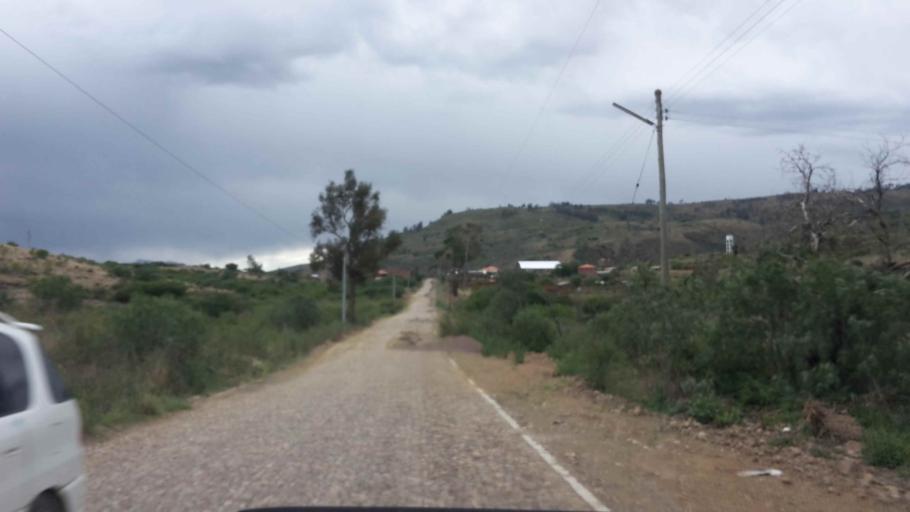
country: BO
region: Cochabamba
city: Cochabamba
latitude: -17.5407
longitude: -66.1981
